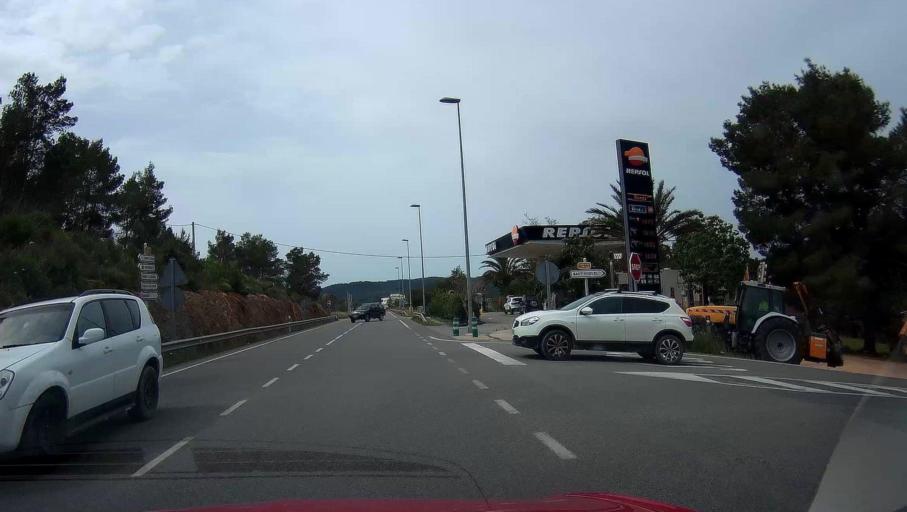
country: ES
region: Balearic Islands
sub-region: Illes Balears
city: Sant Joan de Labritja
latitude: 39.0706
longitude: 1.4966
